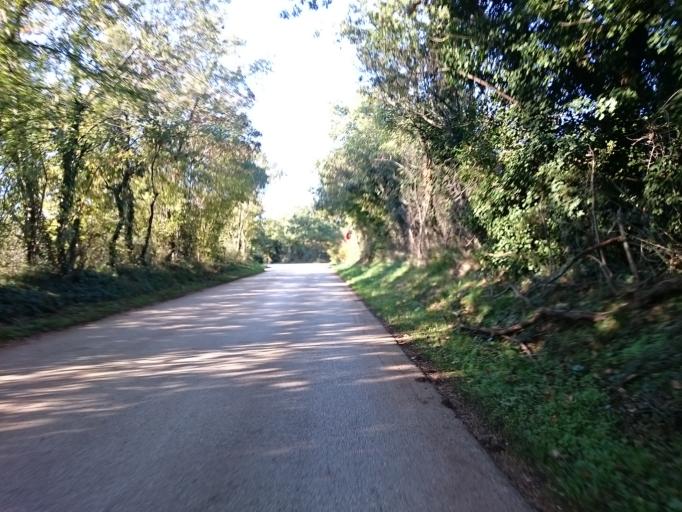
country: HR
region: Istarska
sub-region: Grad Porec
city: Porec
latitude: 45.2778
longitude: 13.6503
